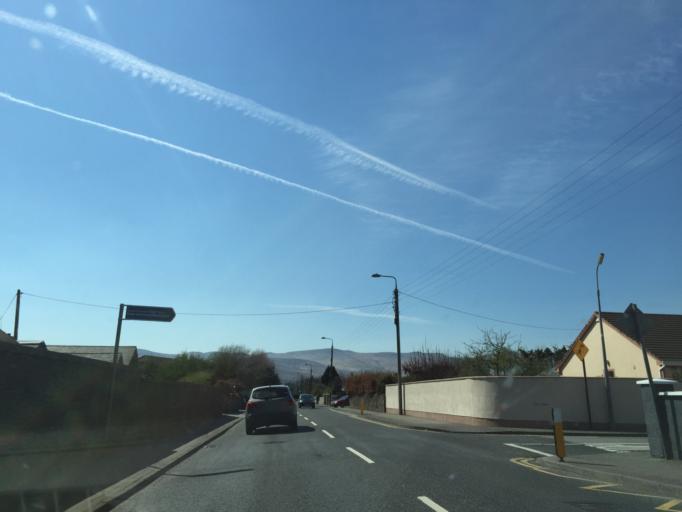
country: IE
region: Munster
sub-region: Ciarrai
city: Tralee
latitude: 52.2630
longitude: -9.6826
